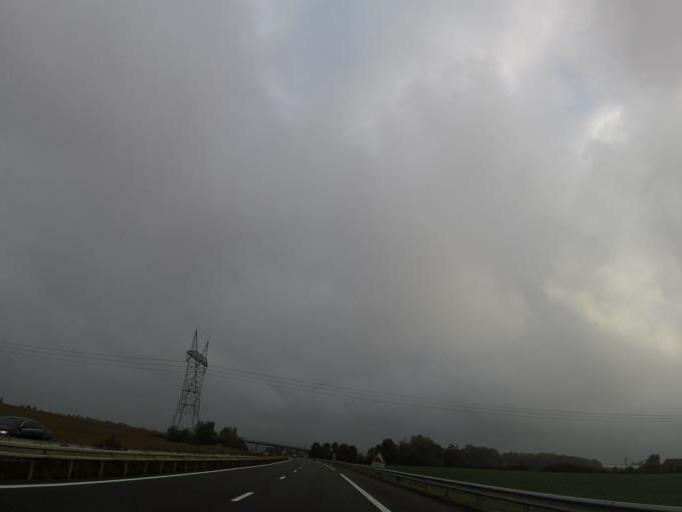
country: FR
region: Ile-de-France
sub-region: Departement de Seine-et-Marne
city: Saint-Jean-les-Deux-Jumeaux
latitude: 48.9316
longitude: 3.0246
